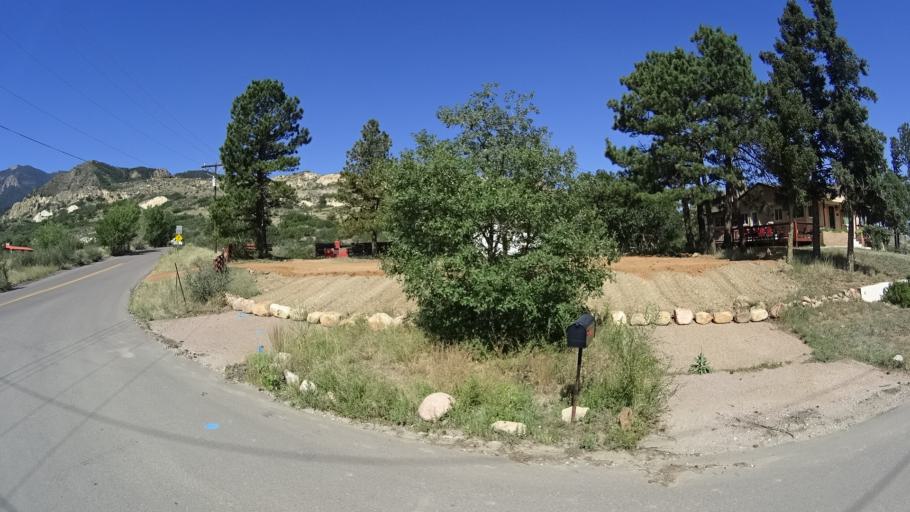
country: US
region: Colorado
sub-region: El Paso County
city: Manitou Springs
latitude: 38.8310
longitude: -104.8786
